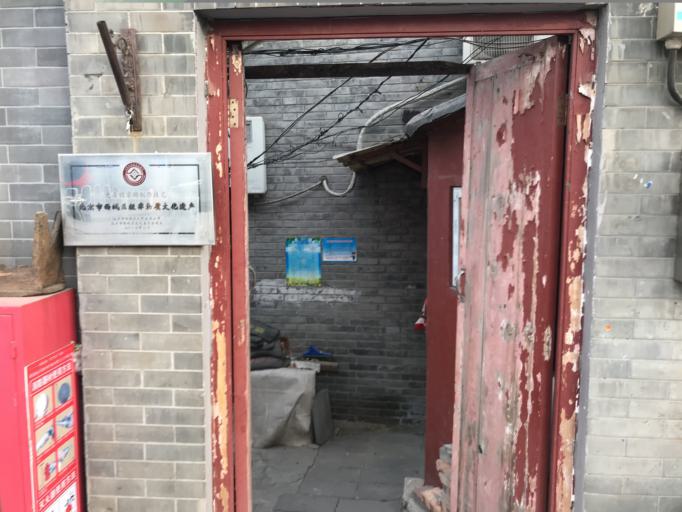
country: CN
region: Beijing
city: Beijing
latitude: 39.8914
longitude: 116.3786
